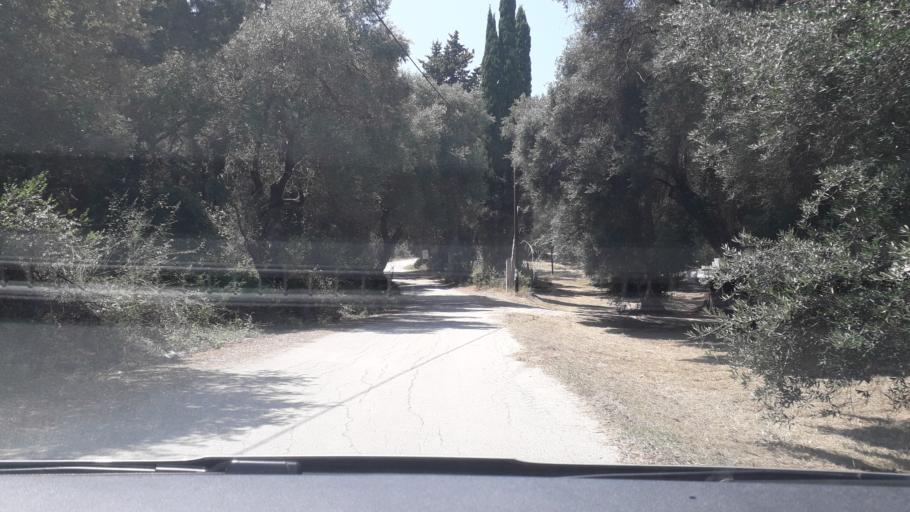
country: GR
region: Ionian Islands
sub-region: Nomos Kerkyras
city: Lefkimmi
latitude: 39.3797
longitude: 20.1090
